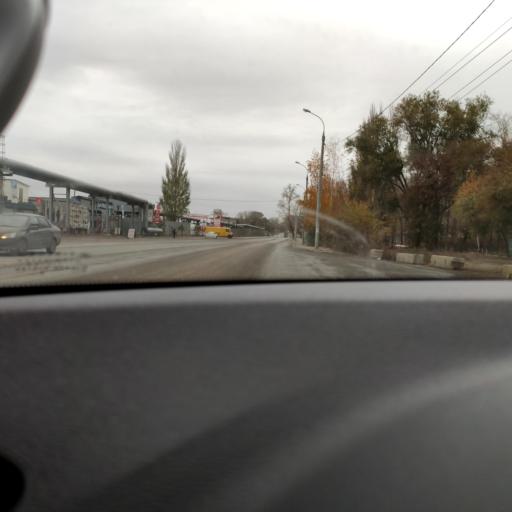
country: RU
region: Samara
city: Smyshlyayevka
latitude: 53.2109
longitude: 50.2978
